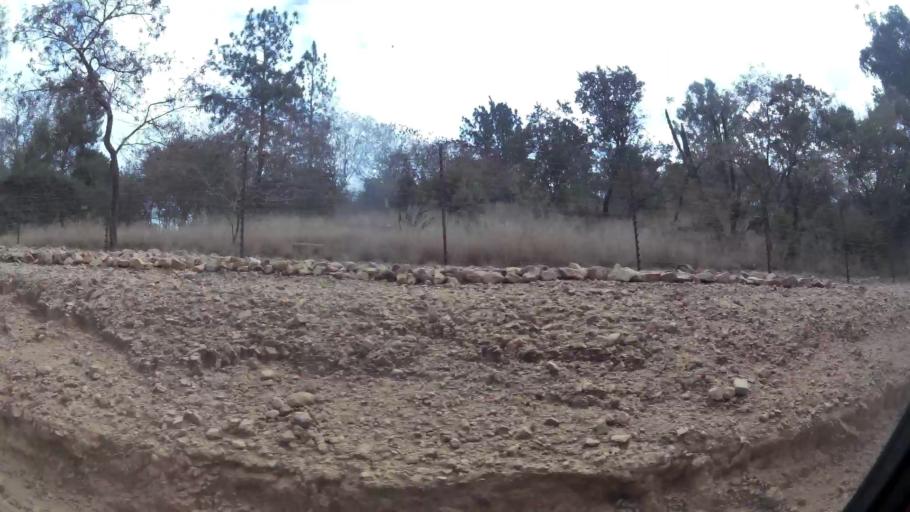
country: ZA
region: Gauteng
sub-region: West Rand District Municipality
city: Muldersdriseloop
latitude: -26.0737
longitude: 27.8787
